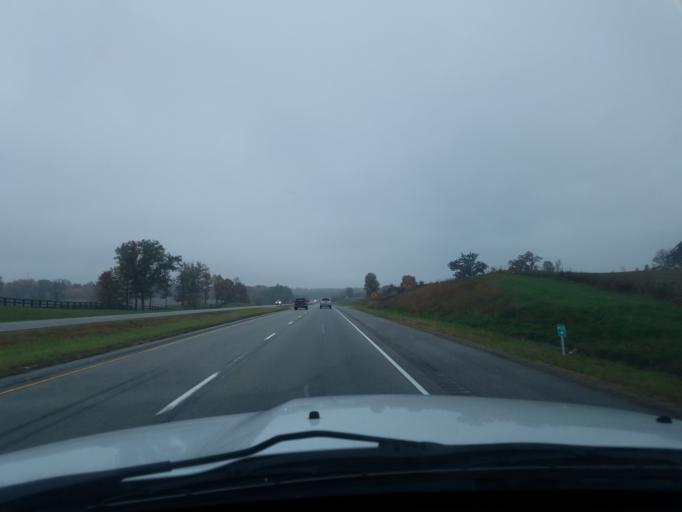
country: US
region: Kentucky
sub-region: Hardin County
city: Elizabethtown
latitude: 37.6545
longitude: -85.8368
